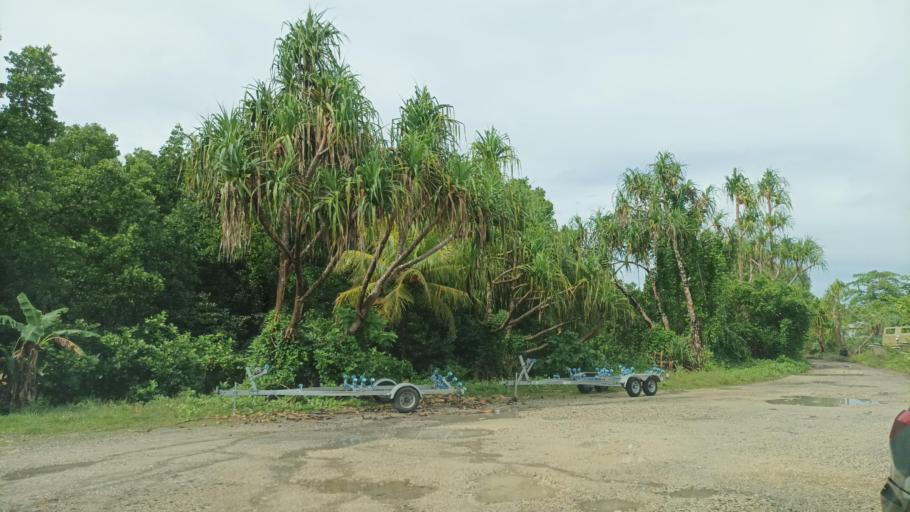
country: FM
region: Kosrae
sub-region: Tafunsak Municipality
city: Tafunsak
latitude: 5.3572
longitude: 162.9644
